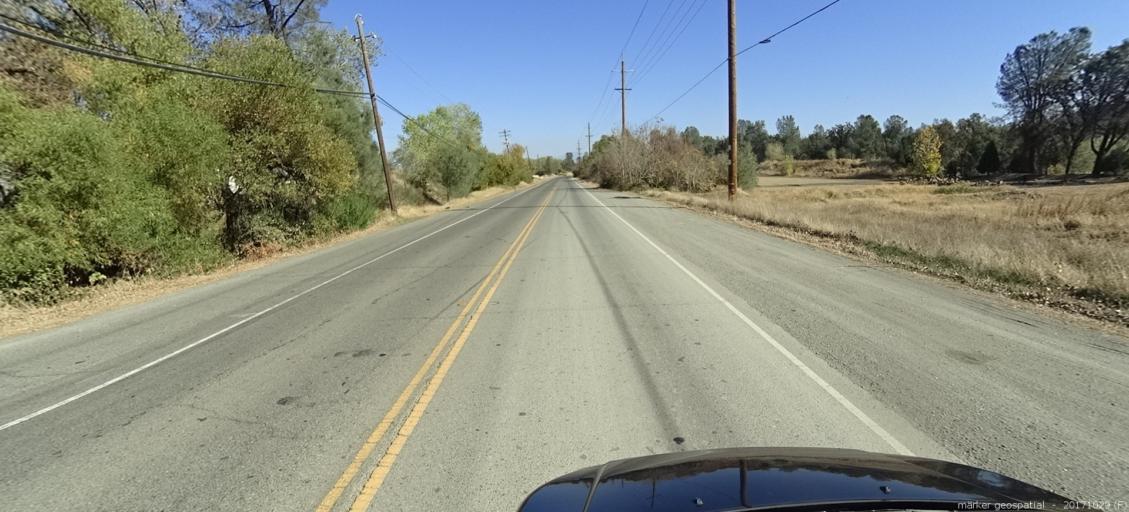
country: US
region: California
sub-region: Shasta County
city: Redding
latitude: 40.5050
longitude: -122.4137
